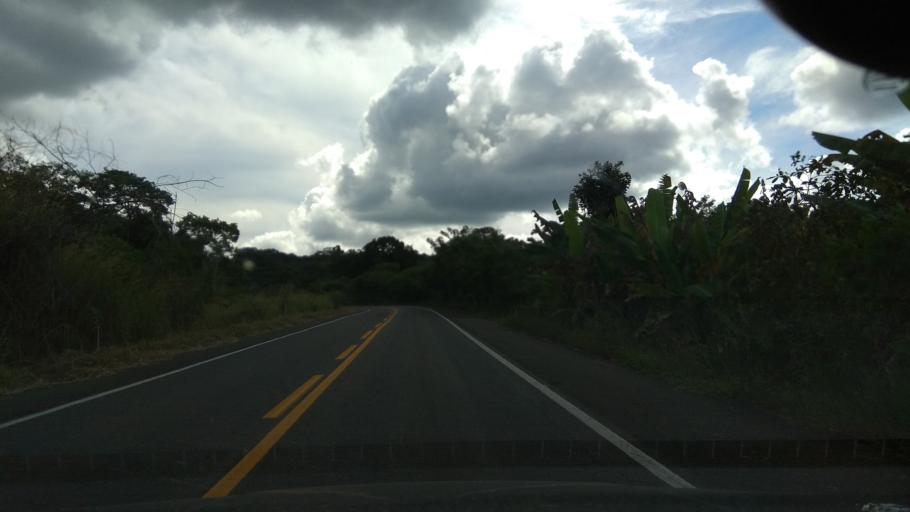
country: BR
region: Bahia
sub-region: Ubaitaba
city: Ubaitaba
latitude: -14.2628
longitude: -39.3327
